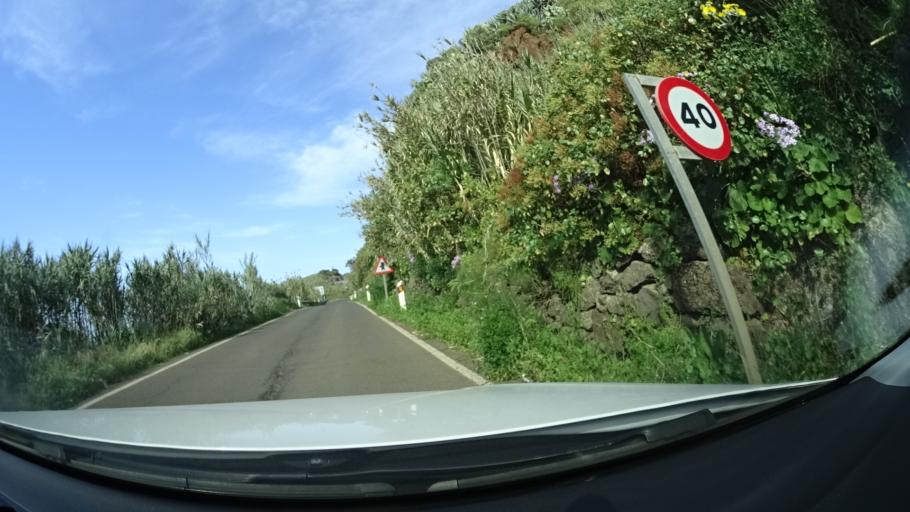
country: ES
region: Canary Islands
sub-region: Provincia de Las Palmas
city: Guia
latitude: 28.1084
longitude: -15.6401
